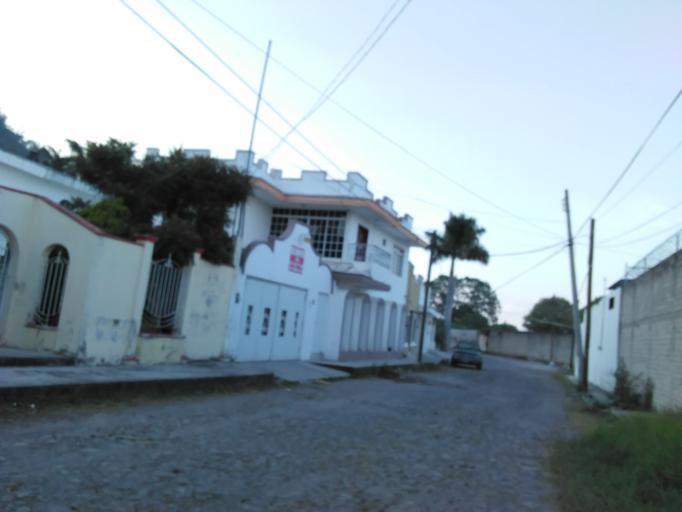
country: MX
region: Nayarit
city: Tepic
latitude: 21.5082
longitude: -104.9205
